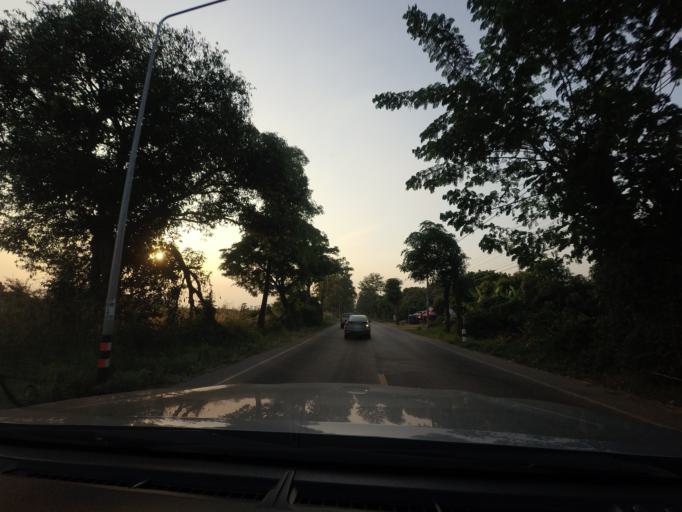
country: TH
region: Phitsanulok
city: Wang Thong
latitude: 16.7370
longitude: 100.4454
